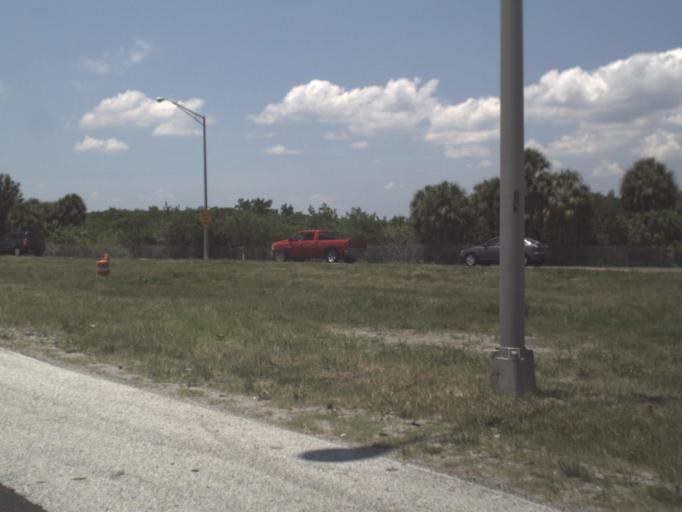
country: US
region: Florida
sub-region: Hillsborough County
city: Town 'n' Country
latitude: 27.9438
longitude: -82.5426
